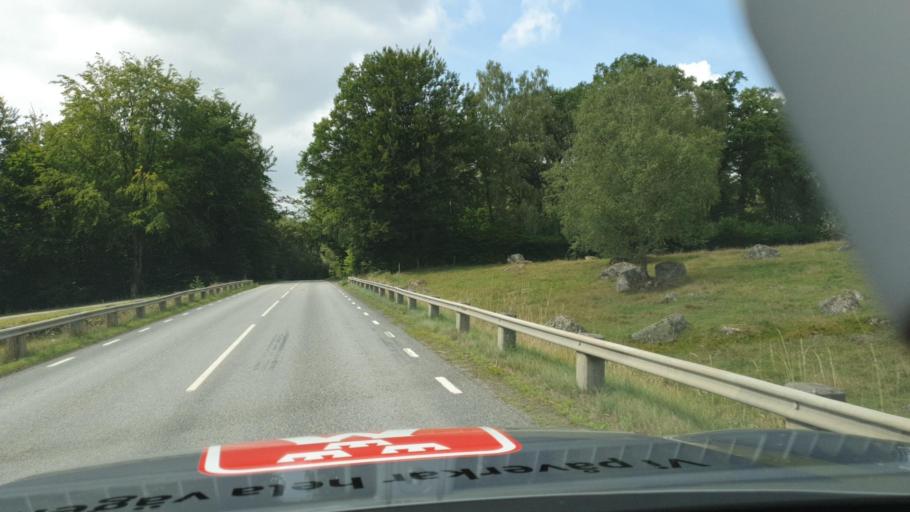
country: SE
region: Skane
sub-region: Ostra Goinge Kommun
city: Knislinge
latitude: 56.1890
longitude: 14.0381
